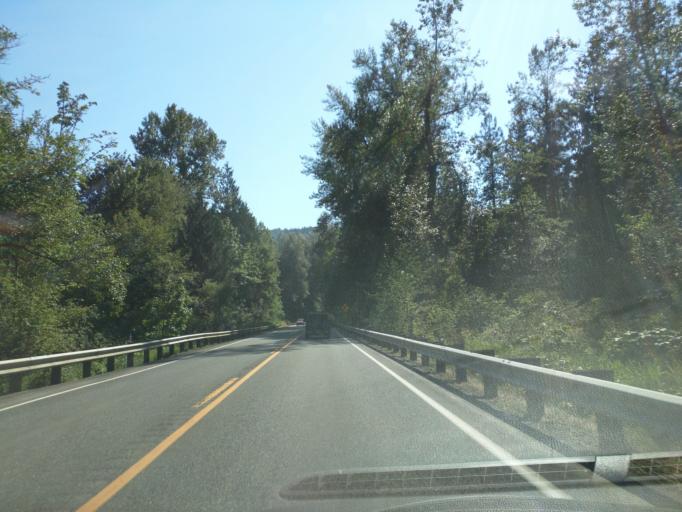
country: US
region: Washington
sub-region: Whatcom County
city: Peaceful Valley
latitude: 48.8181
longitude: -122.1992
